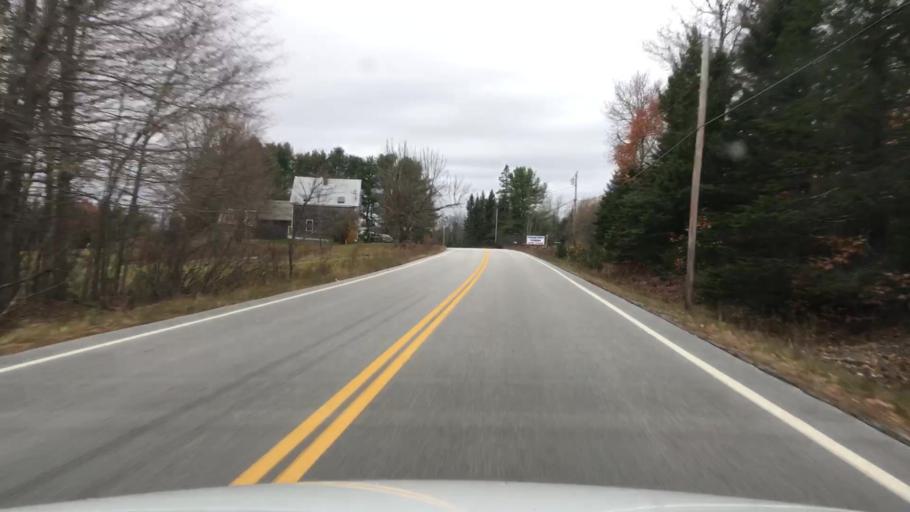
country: US
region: Maine
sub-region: Hancock County
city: Penobscot
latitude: 44.4932
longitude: -68.6444
